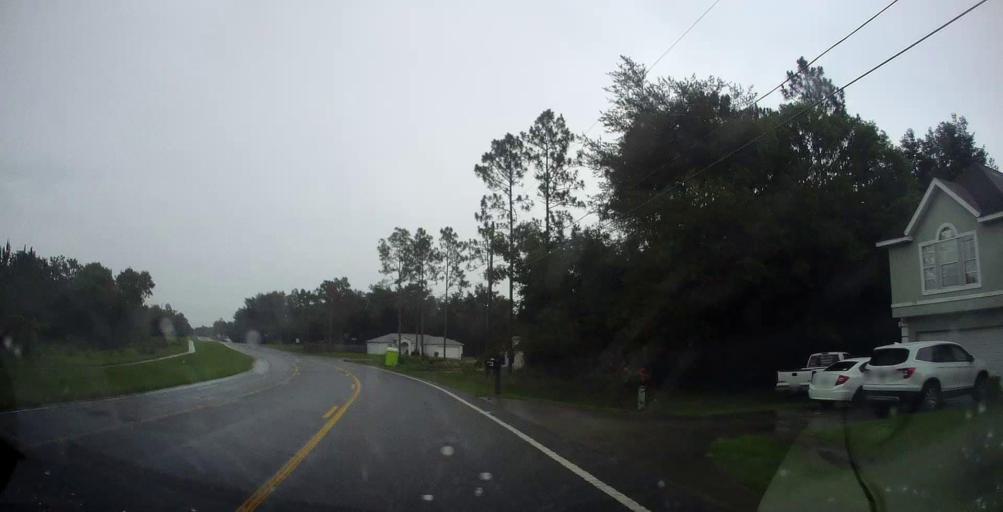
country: US
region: Florida
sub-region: Marion County
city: Silver Springs Shores
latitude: 29.1141
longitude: -82.0185
